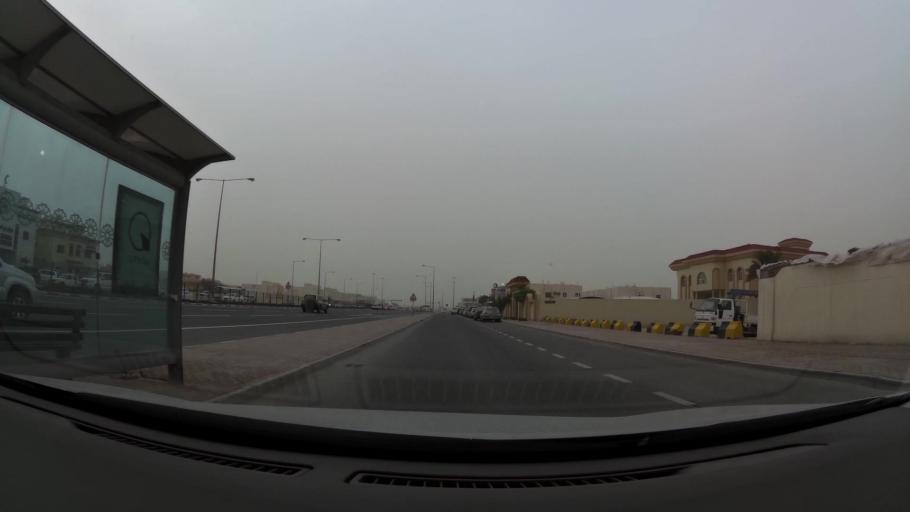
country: QA
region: Baladiyat ad Dawhah
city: Doha
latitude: 25.2363
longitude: 51.5003
